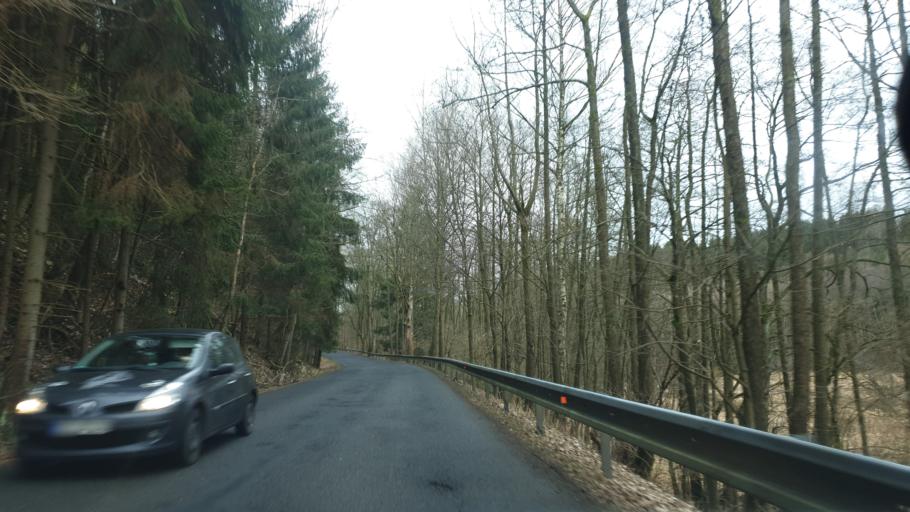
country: DE
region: Saxony
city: Bad Elster
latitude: 50.2668
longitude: 12.2466
